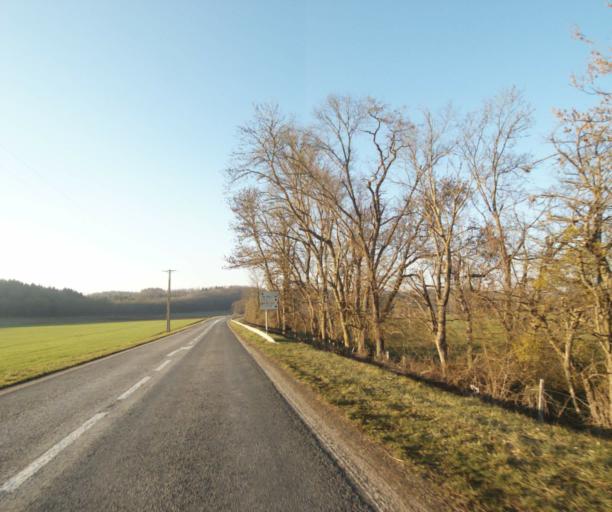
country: FR
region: Champagne-Ardenne
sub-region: Departement de la Haute-Marne
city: Bienville
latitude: 48.5658
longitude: 5.0446
